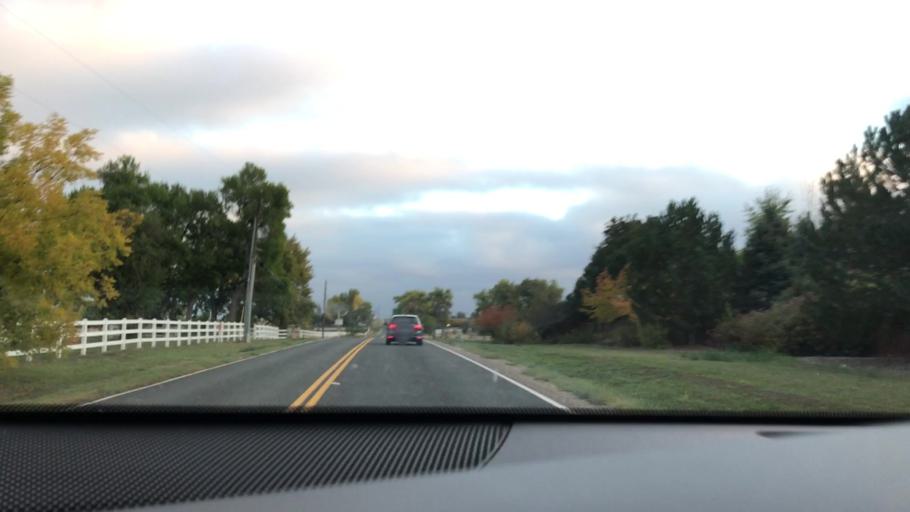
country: US
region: Colorado
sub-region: Broomfield County
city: Broomfield
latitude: 39.9509
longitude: -105.0624
